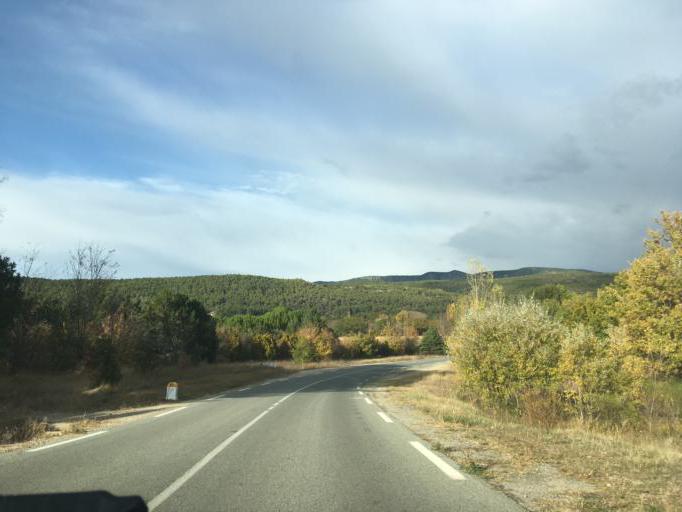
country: FR
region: Provence-Alpes-Cote d'Azur
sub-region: Departement du Var
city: Villecroze
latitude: 43.5703
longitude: 6.2607
